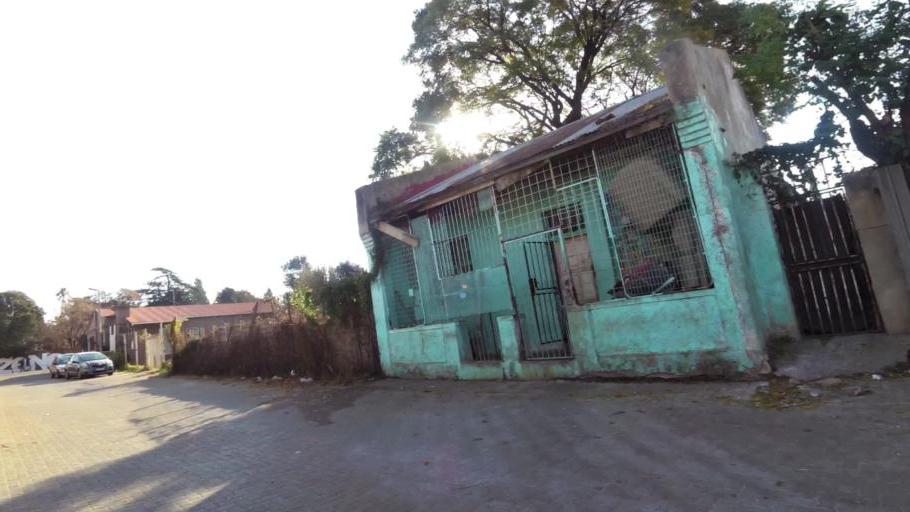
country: ZA
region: Gauteng
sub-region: City of Johannesburg Metropolitan Municipality
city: Johannesburg
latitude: -26.1962
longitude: 28.0159
